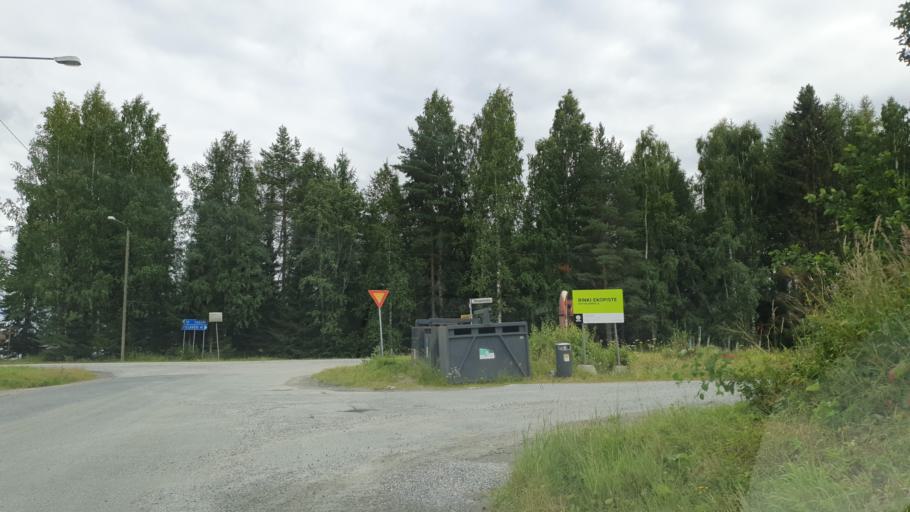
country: FI
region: Northern Savo
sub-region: Ylae-Savo
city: Iisalmi
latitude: 63.5139
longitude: 27.1206
